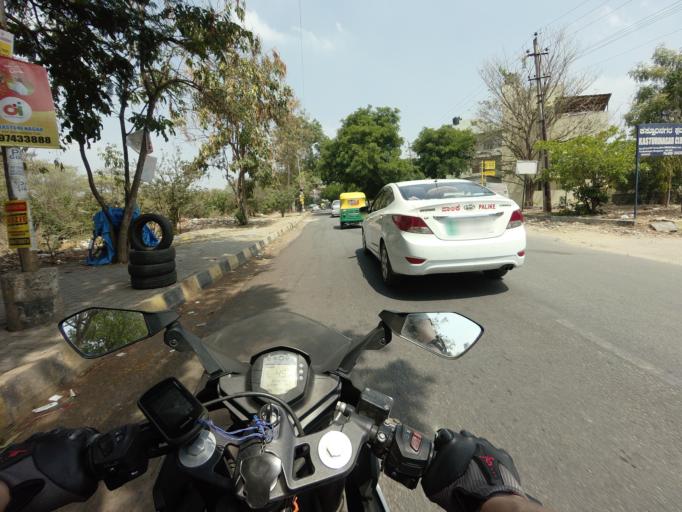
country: IN
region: Karnataka
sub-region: Bangalore Urban
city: Bangalore
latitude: 13.0038
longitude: 77.6572
